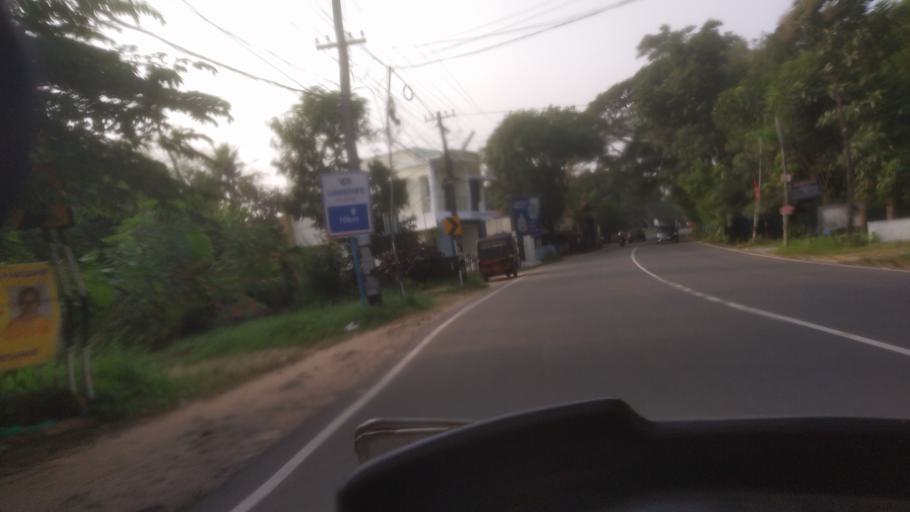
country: IN
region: Kerala
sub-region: Alappuzha
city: Arukutti
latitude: 9.8893
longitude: 76.3729
